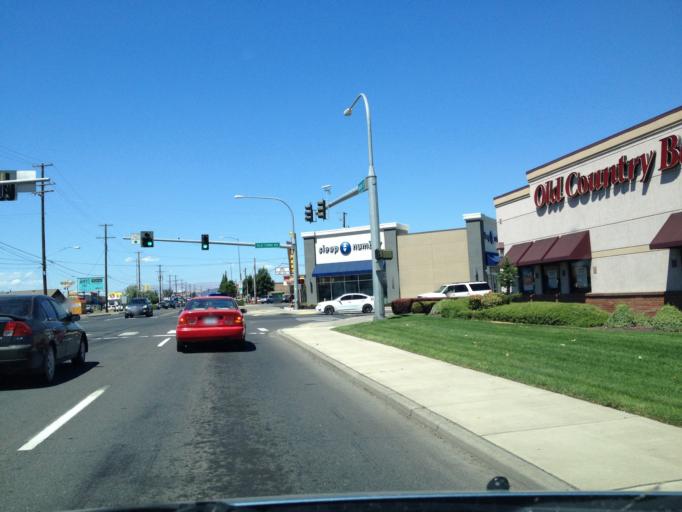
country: US
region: Washington
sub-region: Yakima County
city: Union Gap
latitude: 46.5654
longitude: -120.4820
